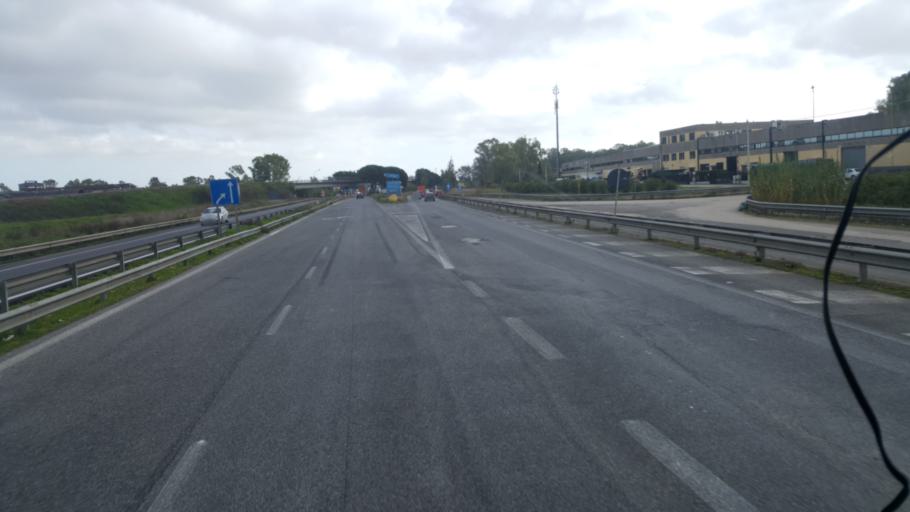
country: IT
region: Latium
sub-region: Provincia di Latina
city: Borgo Podgora
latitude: 41.4847
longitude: 12.8562
